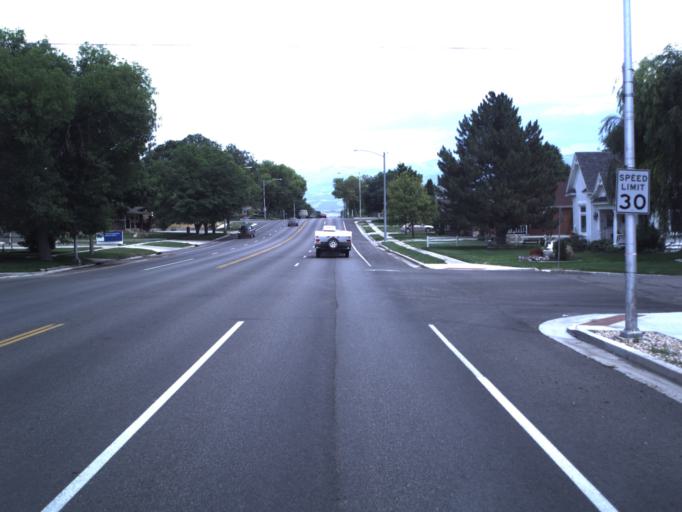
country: US
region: Utah
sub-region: Sanpete County
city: Moroni
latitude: 39.5249
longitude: -111.5842
